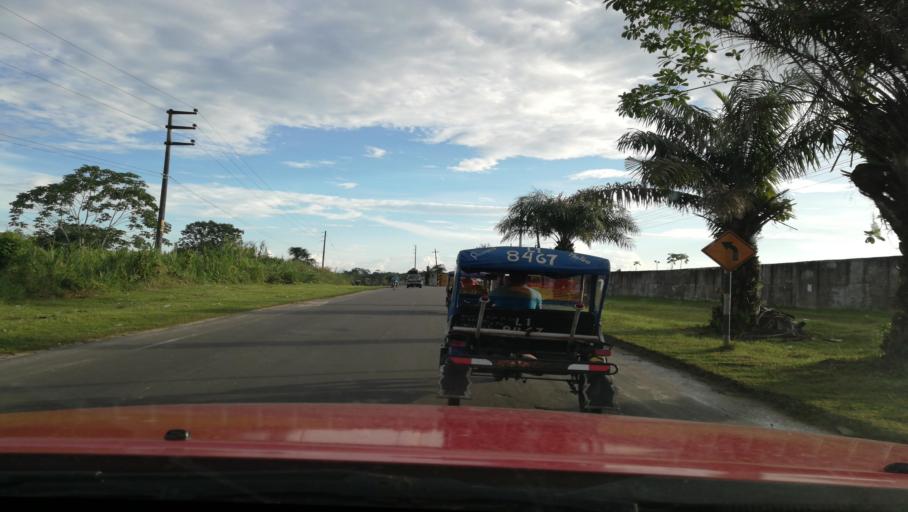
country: PE
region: Loreto
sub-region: Provincia de Maynas
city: Iquitos
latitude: -3.8304
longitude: -73.3274
